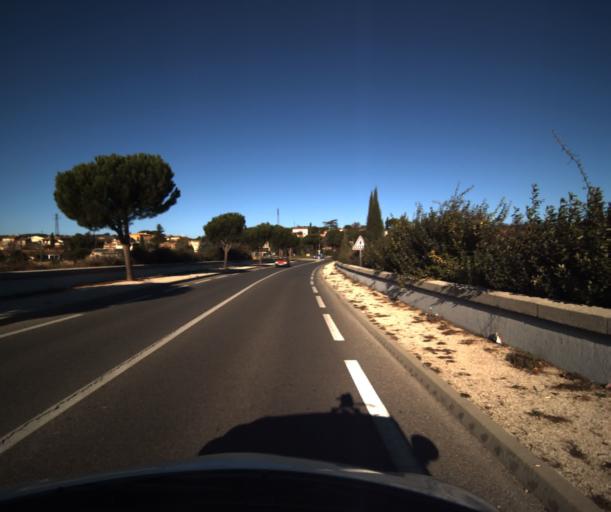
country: FR
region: Provence-Alpes-Cote d'Azur
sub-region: Departement du Vaucluse
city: Pertuis
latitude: 43.7023
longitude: 5.5099
